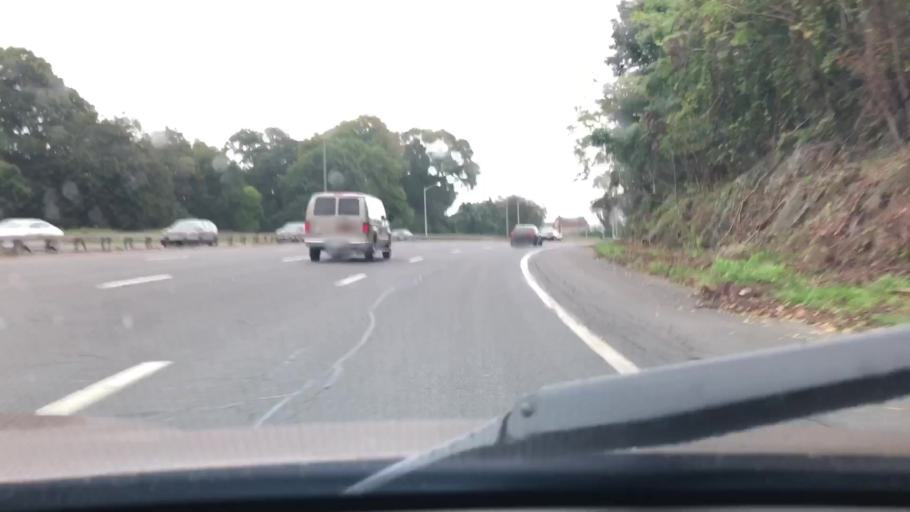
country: US
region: New York
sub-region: Westchester County
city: Yonkers
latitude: 40.9345
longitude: -73.8656
